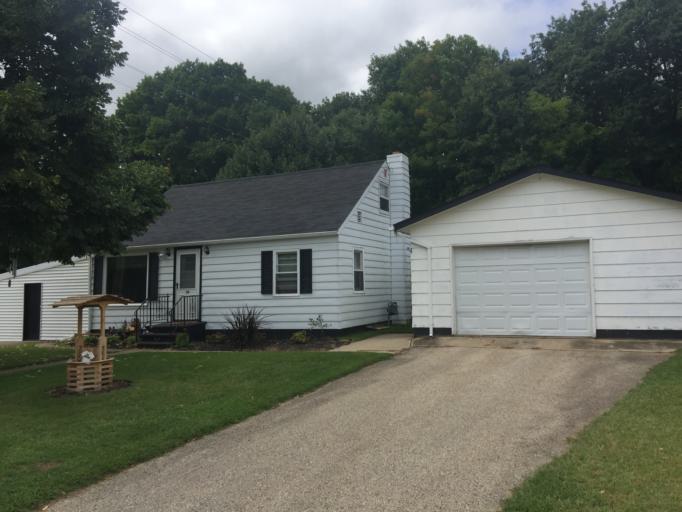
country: US
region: Wisconsin
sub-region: Oconto County
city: Oconto Falls
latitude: 44.8683
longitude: -88.1320
